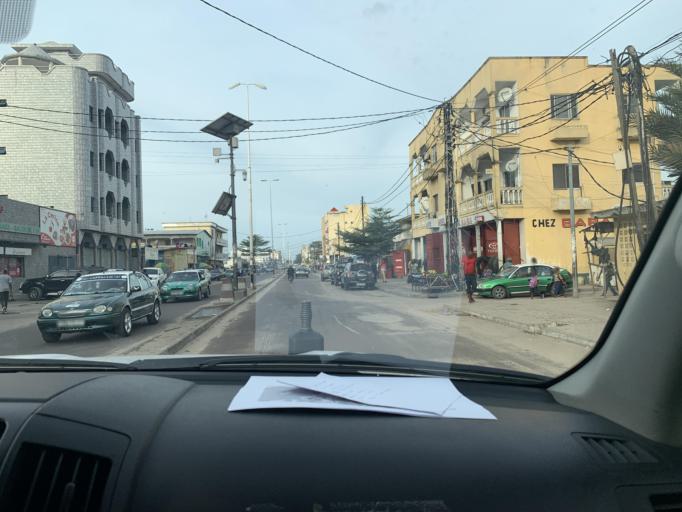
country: CG
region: Brazzaville
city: Brazzaville
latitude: -4.2513
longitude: 15.2772
